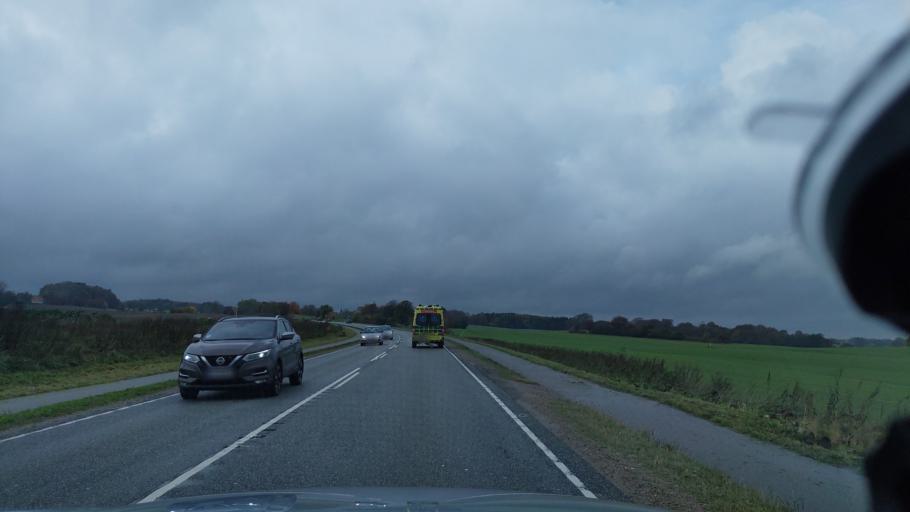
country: DK
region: Zealand
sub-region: Faxe Kommune
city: Ronnede
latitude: 55.2618
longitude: 11.9778
